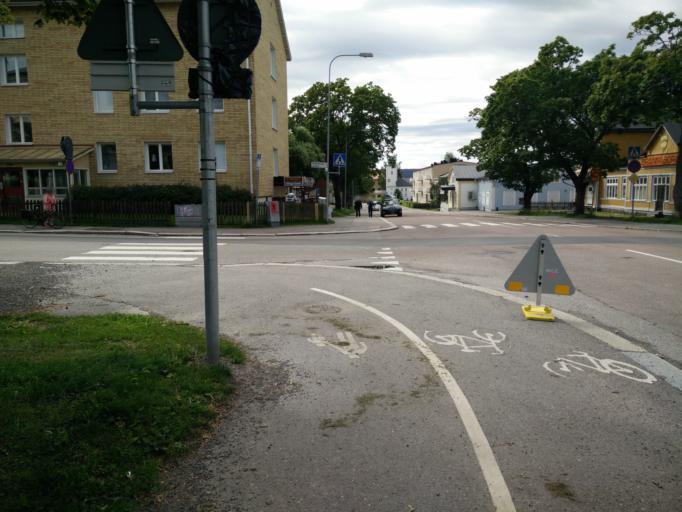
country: SE
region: Vaesternorrland
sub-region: Haernoesands Kommun
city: Haernoesand
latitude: 62.6356
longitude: 17.9485
